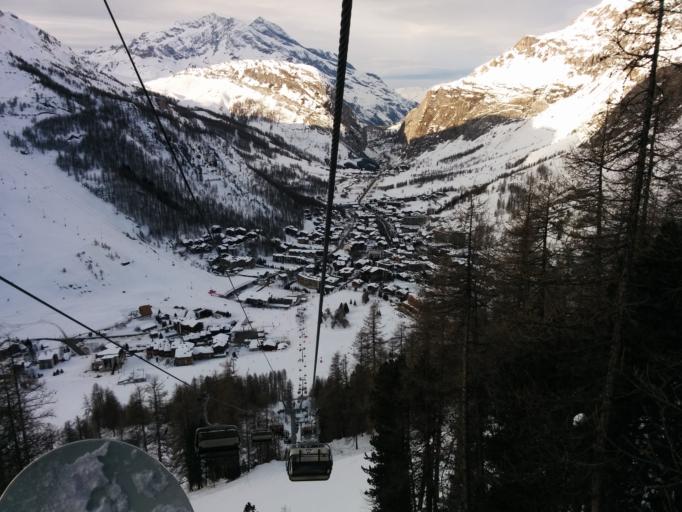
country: FR
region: Rhone-Alpes
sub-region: Departement de la Savoie
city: Val-d'Isere
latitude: 45.4415
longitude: 6.9841
